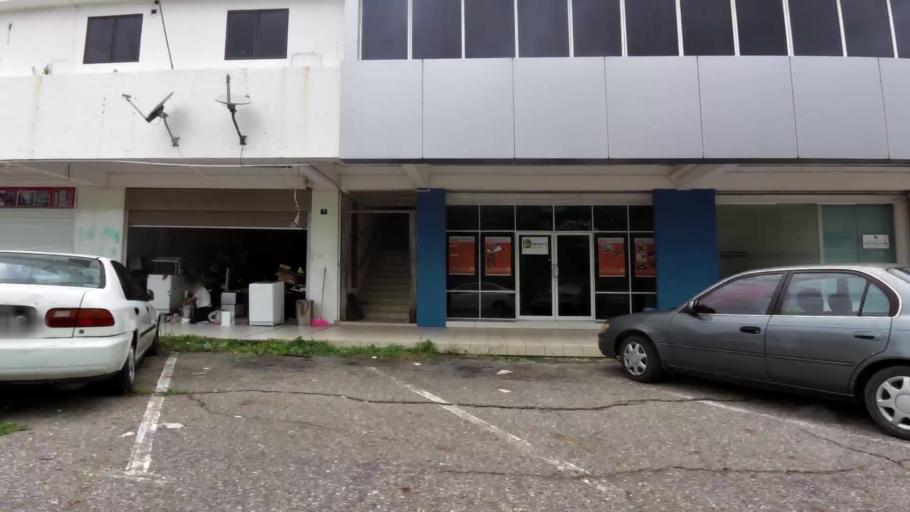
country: BN
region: Brunei and Muara
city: Bandar Seri Begawan
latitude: 4.9078
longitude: 114.9140
